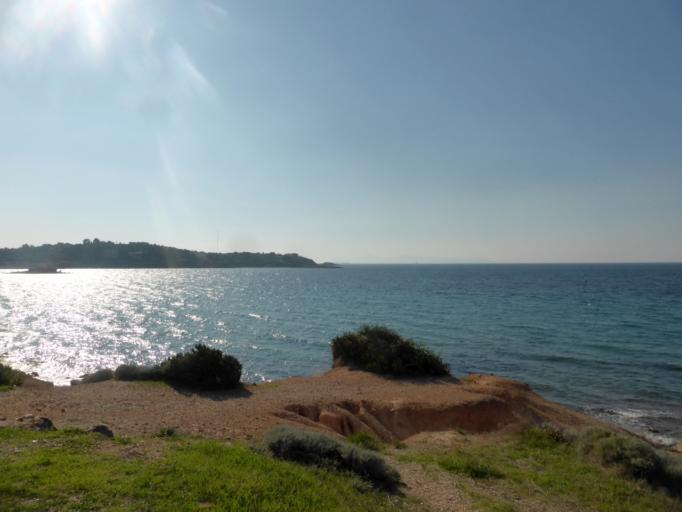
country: GR
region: Attica
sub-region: Nomarchia Anatolikis Attikis
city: Vouliagmeni
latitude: 37.8229
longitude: 23.7694
